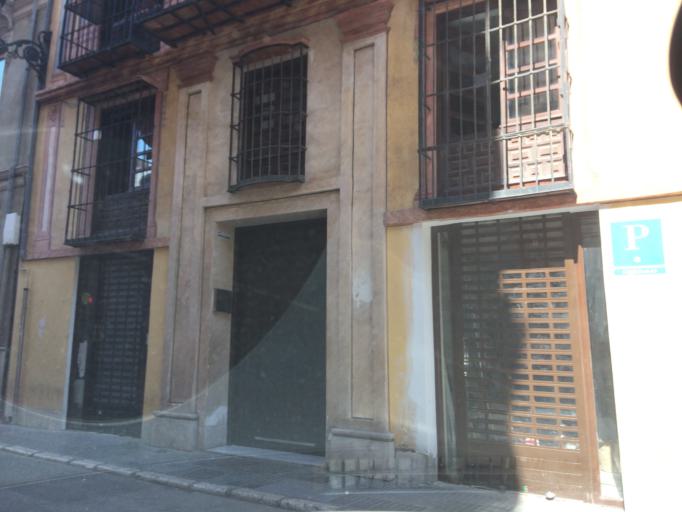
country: ES
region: Andalusia
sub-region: Provincia de Malaga
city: Malaga
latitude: 36.7178
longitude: -4.4240
